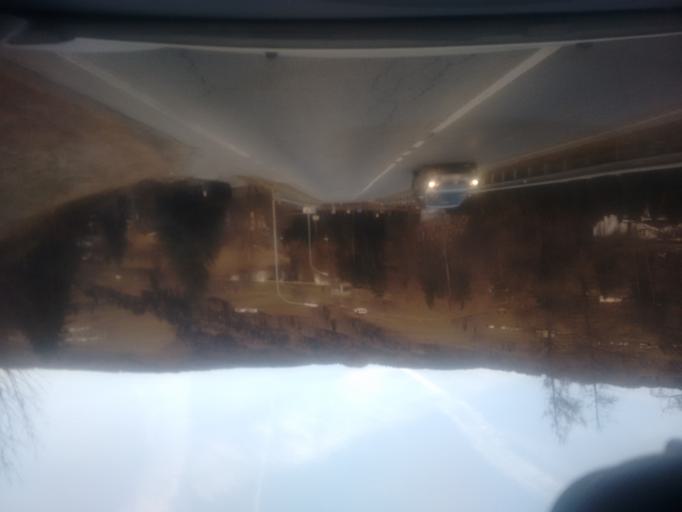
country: IT
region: Trentino-Alto Adige
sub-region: Bolzano
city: Vipiteno
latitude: 46.9017
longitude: 11.4311
